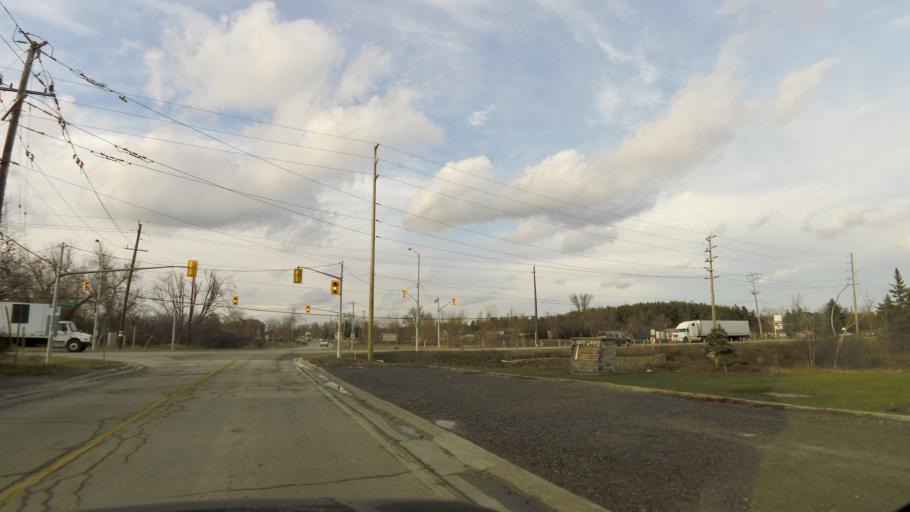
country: CA
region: Ontario
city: Brampton
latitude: 43.8193
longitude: -79.7269
